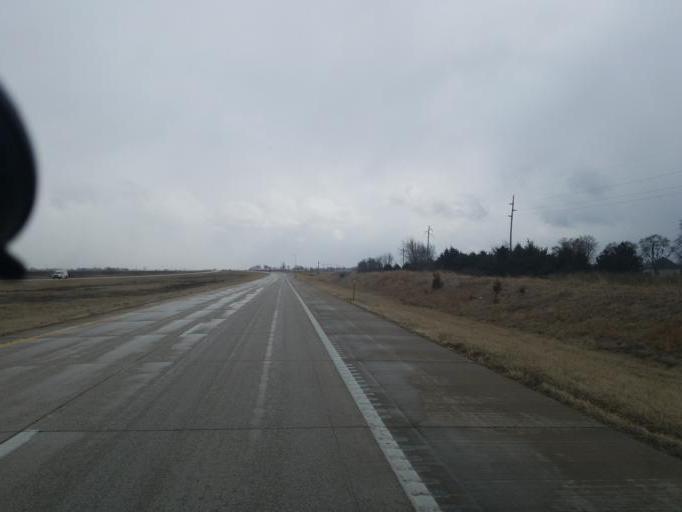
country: US
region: Missouri
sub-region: Randolph County
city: Moberly
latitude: 39.5355
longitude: -92.4470
